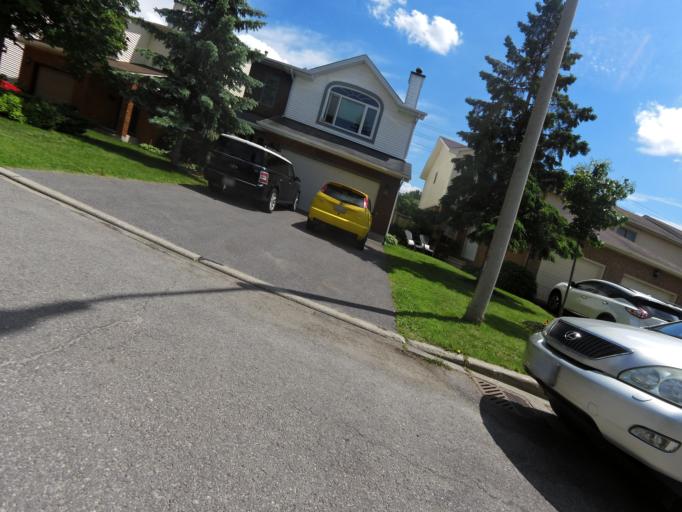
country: CA
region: Ontario
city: Ottawa
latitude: 45.3621
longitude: -75.6278
